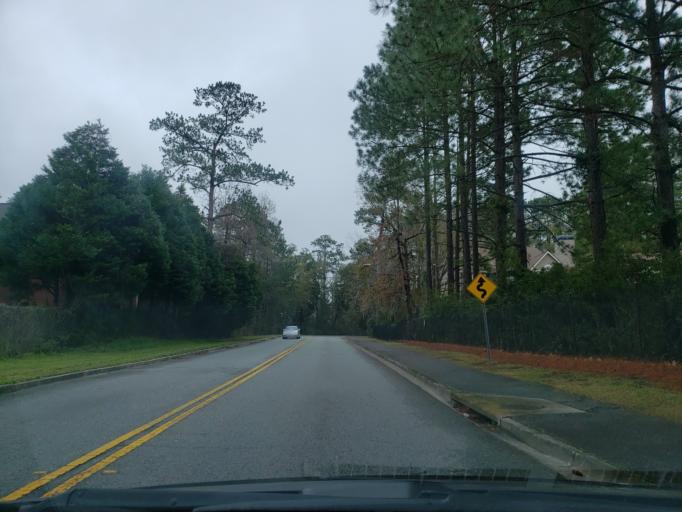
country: US
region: Georgia
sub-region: Chatham County
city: Georgetown
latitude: 31.9768
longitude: -81.1691
